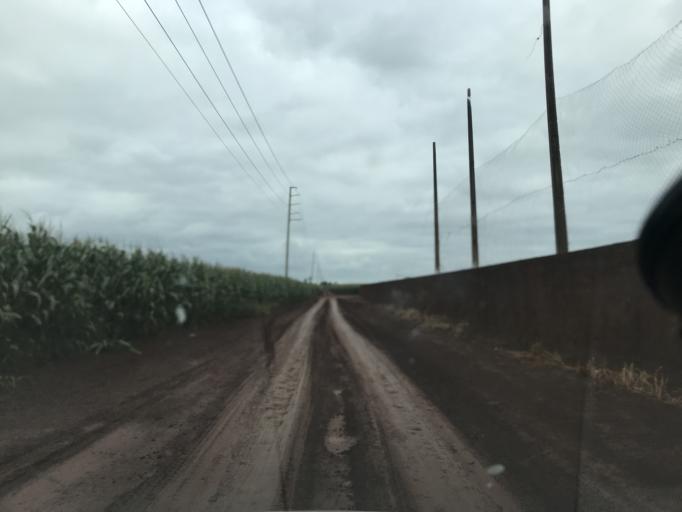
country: BR
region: Parana
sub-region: Palotina
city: Palotina
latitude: -24.3062
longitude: -53.8226
